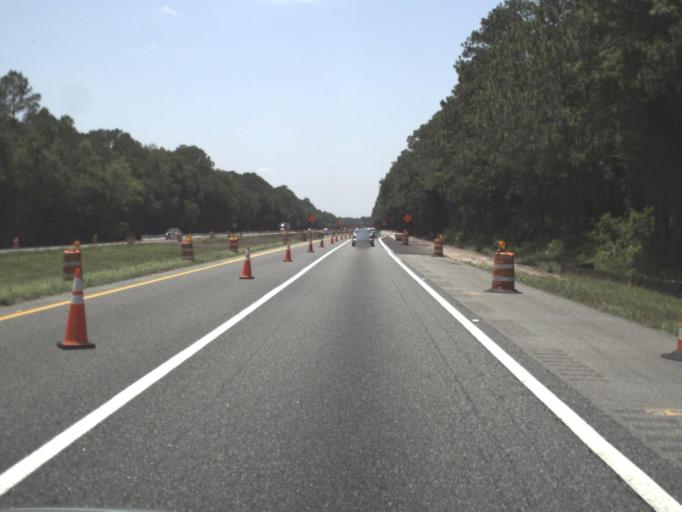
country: US
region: Florida
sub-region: Columbia County
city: Watertown
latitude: 30.2460
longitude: -82.5587
